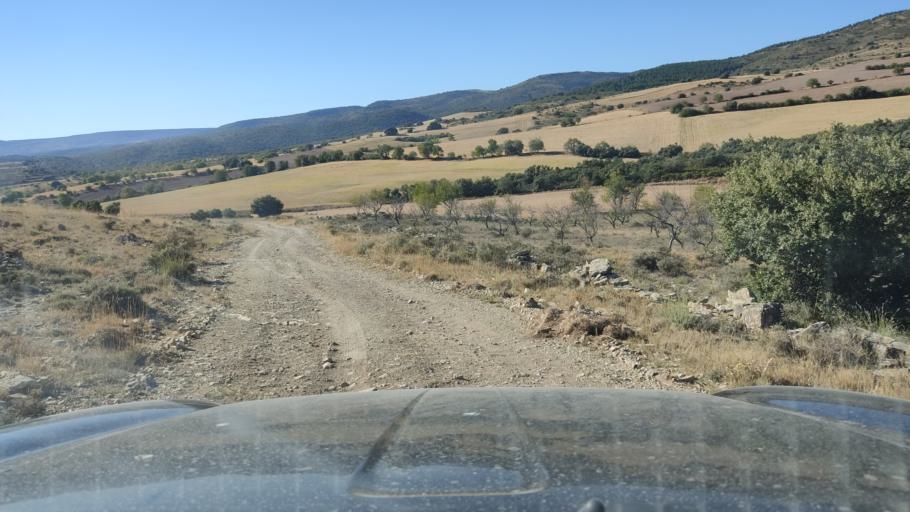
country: ES
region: Aragon
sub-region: Provincia de Teruel
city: Monforte de Moyuela
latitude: 41.0325
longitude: -1.0139
